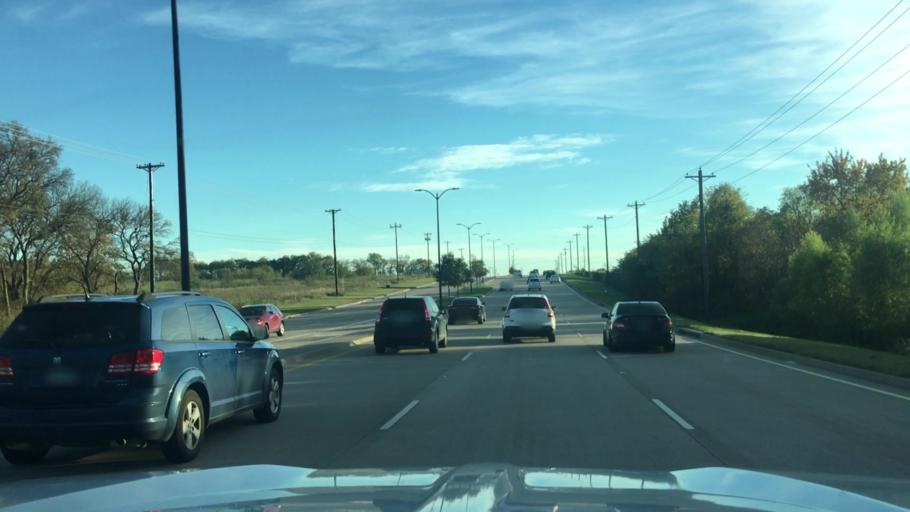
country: US
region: Texas
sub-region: Collin County
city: Prosper
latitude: 33.1965
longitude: -96.8029
